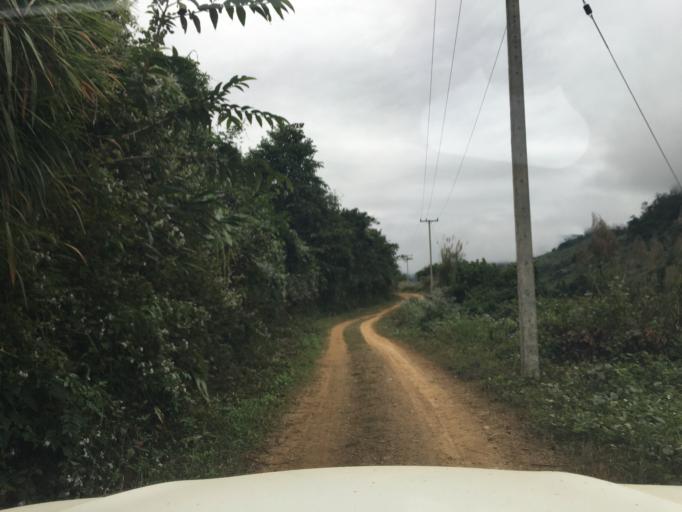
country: LA
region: Houaphan
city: Viengthong
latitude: 19.9436
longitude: 103.2979
